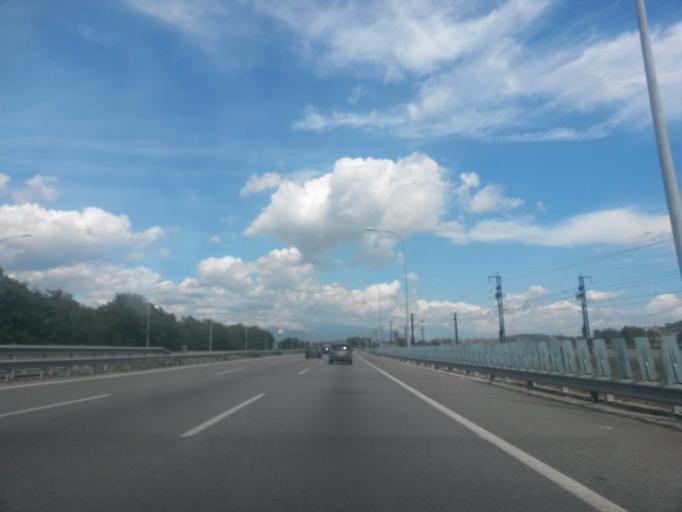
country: ES
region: Catalonia
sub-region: Provincia de Barcelona
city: Mollet del Valles
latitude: 41.5321
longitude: 2.2205
